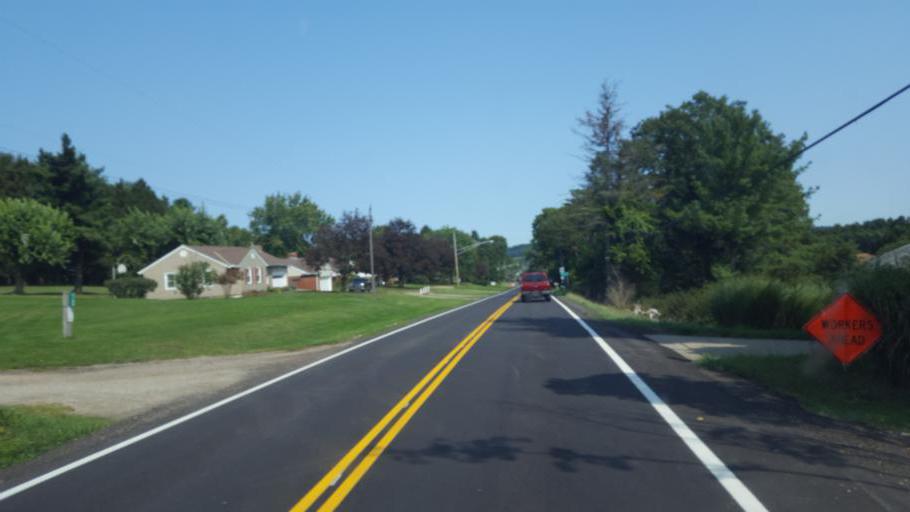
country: US
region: Ohio
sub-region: Richland County
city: Lexington
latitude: 40.6704
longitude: -82.5835
